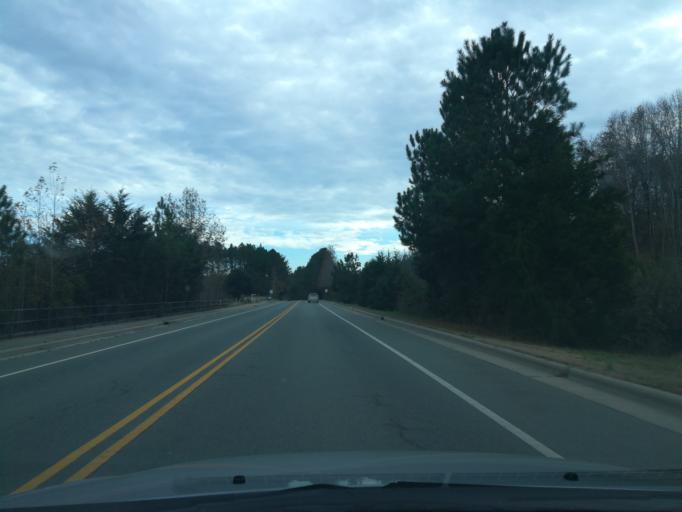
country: US
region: North Carolina
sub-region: Orange County
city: Carrboro
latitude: 35.9738
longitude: -79.0762
